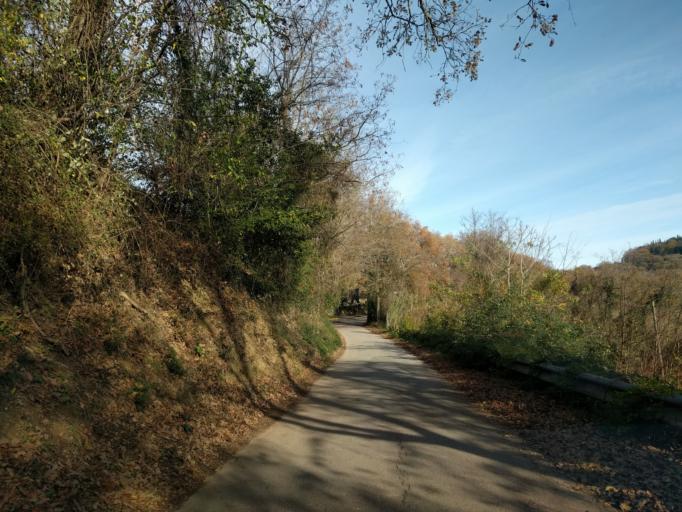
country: IT
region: The Marches
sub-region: Provincia di Pesaro e Urbino
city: Cuccurano
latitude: 43.8132
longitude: 12.9665
